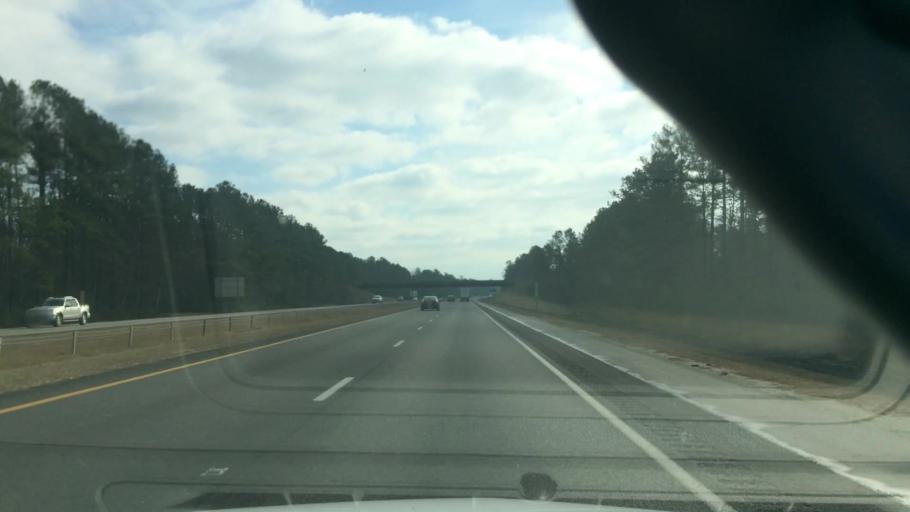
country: US
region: North Carolina
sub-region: Pender County
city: Burgaw
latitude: 34.5683
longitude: -77.8989
